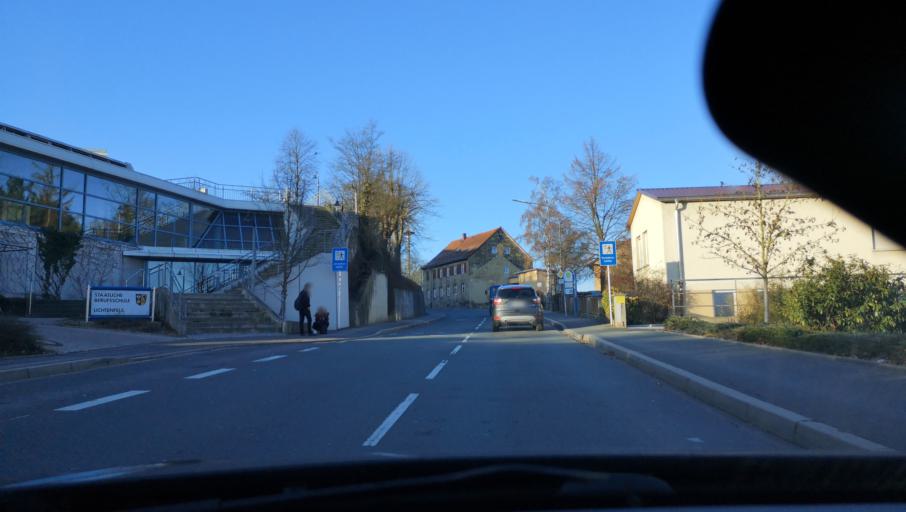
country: DE
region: Bavaria
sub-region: Upper Franconia
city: Lichtenfels
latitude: 50.1460
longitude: 11.0667
